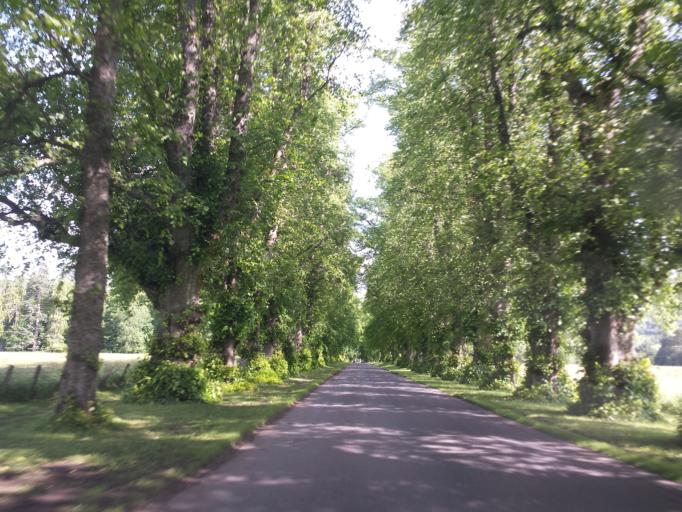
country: GB
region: Scotland
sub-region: Perth and Kinross
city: Pitlochry
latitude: 56.7714
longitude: -3.8532
